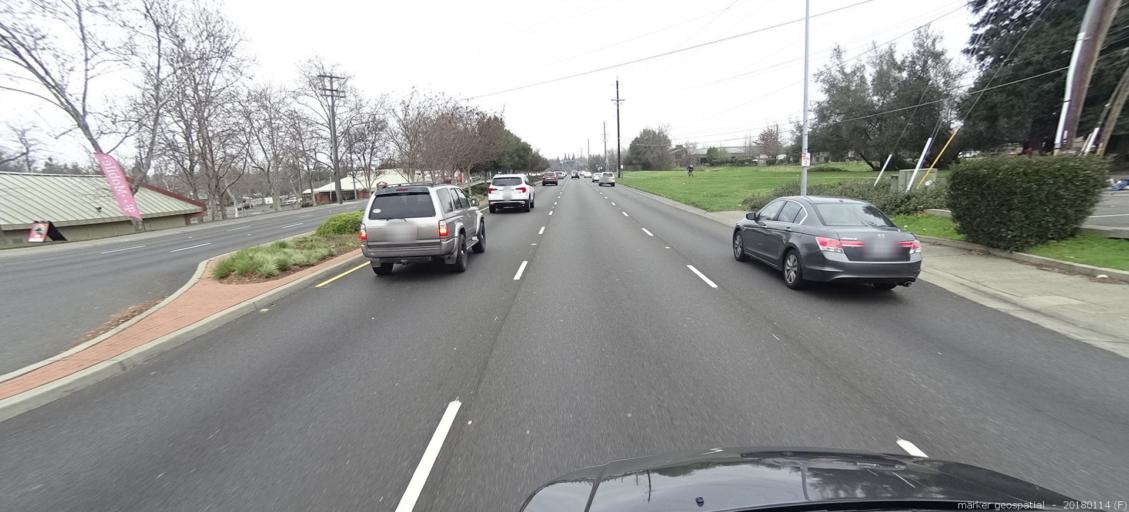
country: US
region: California
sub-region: Sacramento County
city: Gold River
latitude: 38.6208
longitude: -121.2673
